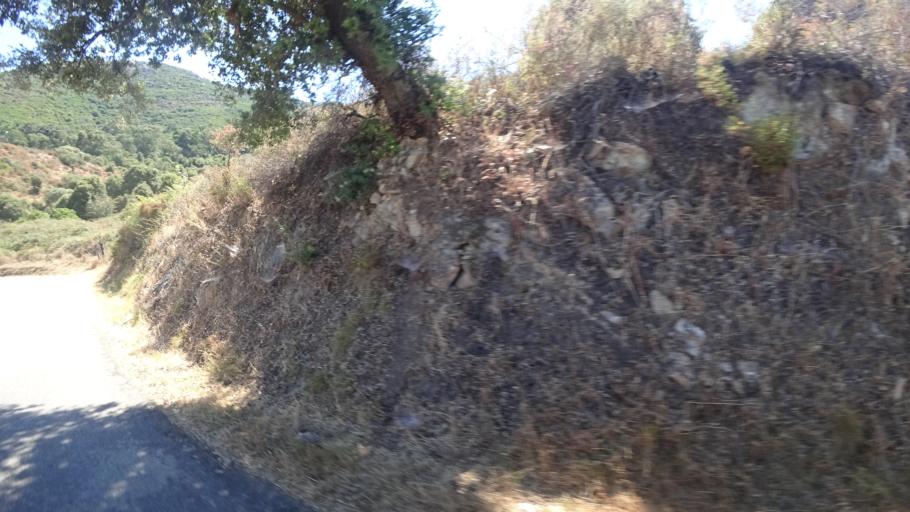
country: FR
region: Corsica
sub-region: Departement de la Corse-du-Sud
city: Alata
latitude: 41.9682
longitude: 8.7019
